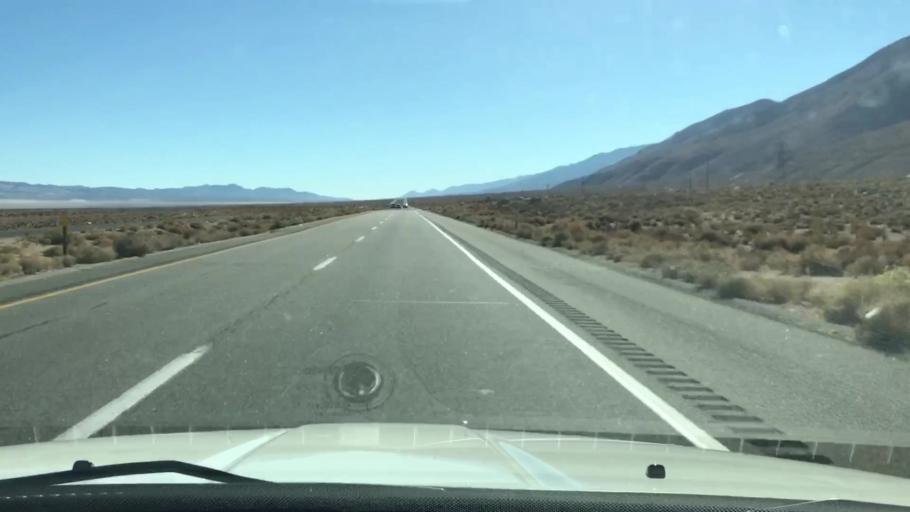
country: US
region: California
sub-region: Inyo County
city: Lone Pine
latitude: 36.4262
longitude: -118.0309
